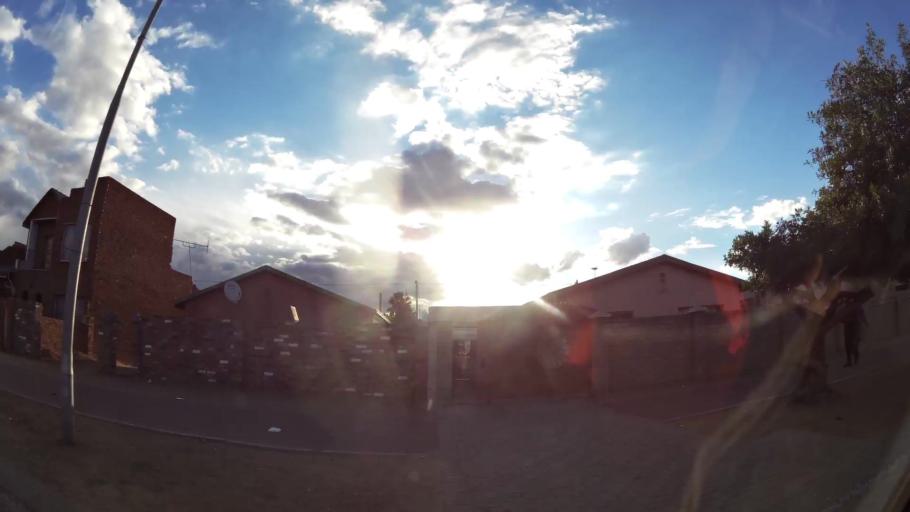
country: ZA
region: Limpopo
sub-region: Capricorn District Municipality
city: Polokwane
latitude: -23.9052
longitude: 29.4301
